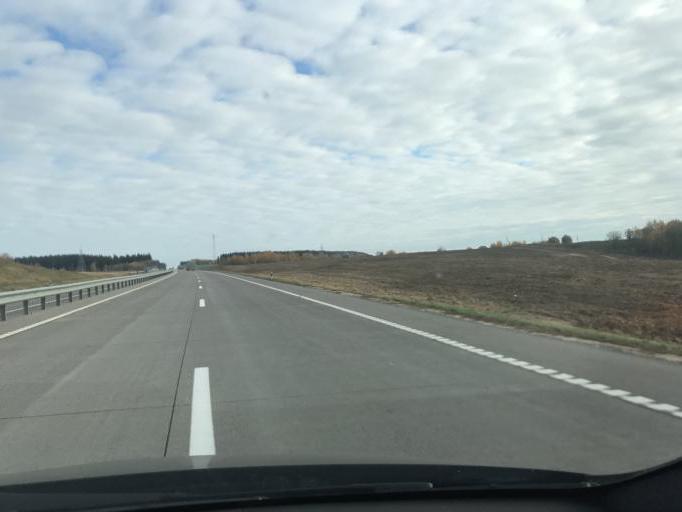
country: BY
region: Minsk
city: Pyatryshki
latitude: 54.0595
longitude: 27.2285
